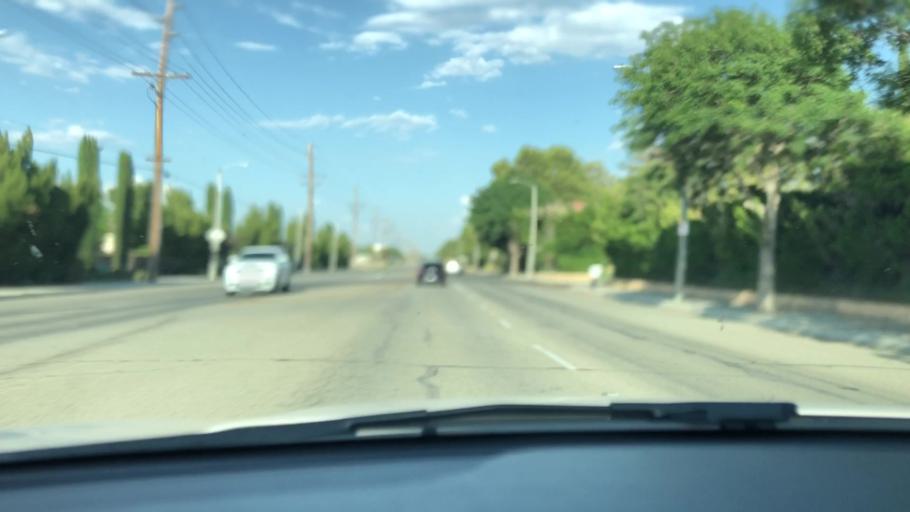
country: US
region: California
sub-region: Los Angeles County
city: Quartz Hill
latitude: 34.6747
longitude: -118.1992
